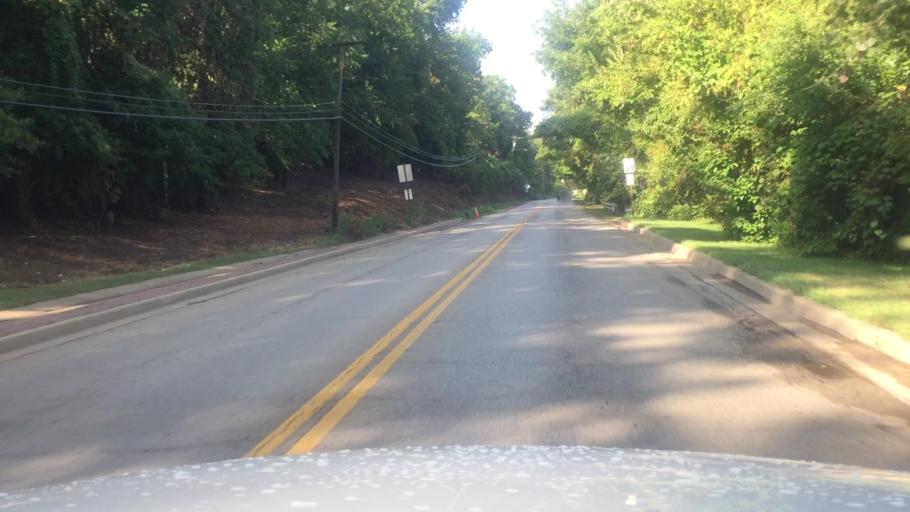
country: US
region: Kansas
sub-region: Wyandotte County
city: Edwardsville
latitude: 39.0501
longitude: -94.7704
